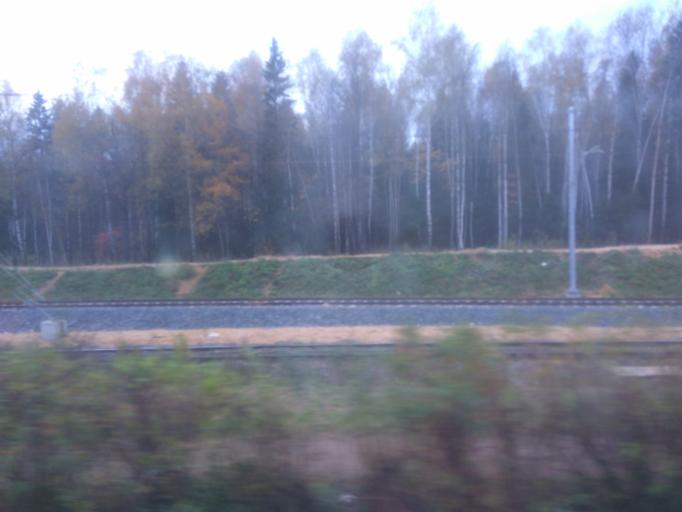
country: RU
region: Moskovskaya
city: Aprelevka
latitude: 55.5636
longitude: 37.0911
